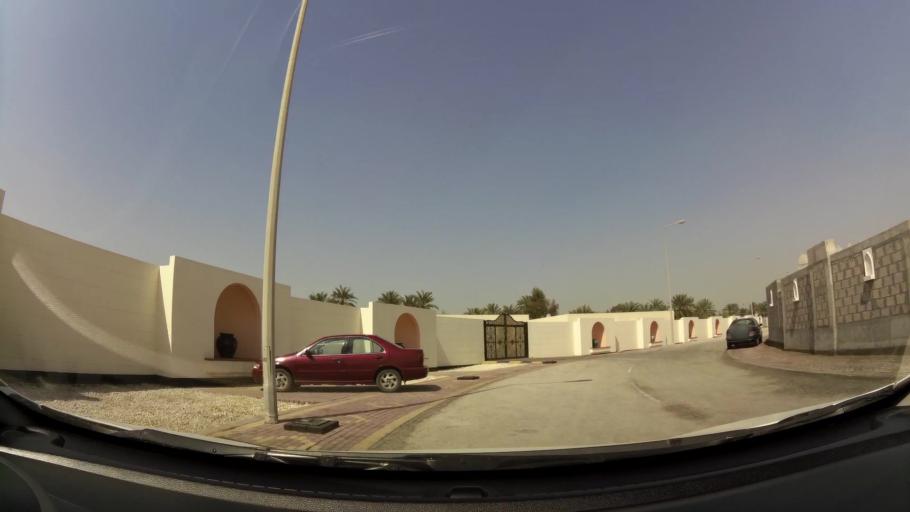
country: BH
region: Central Governorate
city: Madinat Hamad
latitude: 26.1899
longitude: 50.4568
